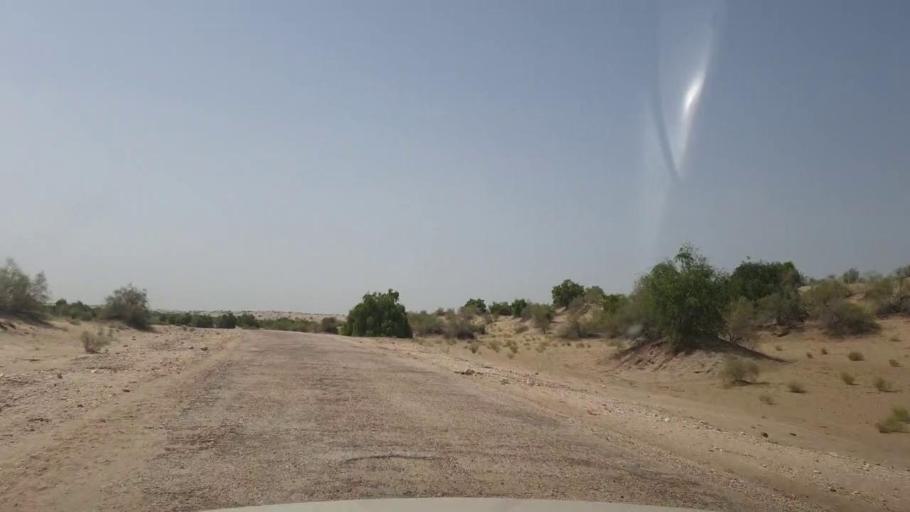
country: PK
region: Sindh
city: Rohri
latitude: 27.4556
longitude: 69.2241
